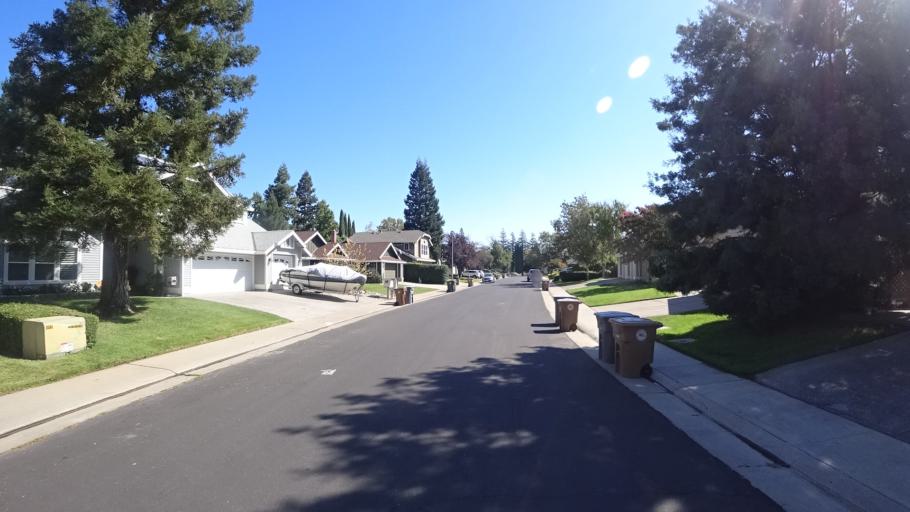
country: US
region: California
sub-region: Sacramento County
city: Laguna
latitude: 38.4246
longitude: -121.4367
